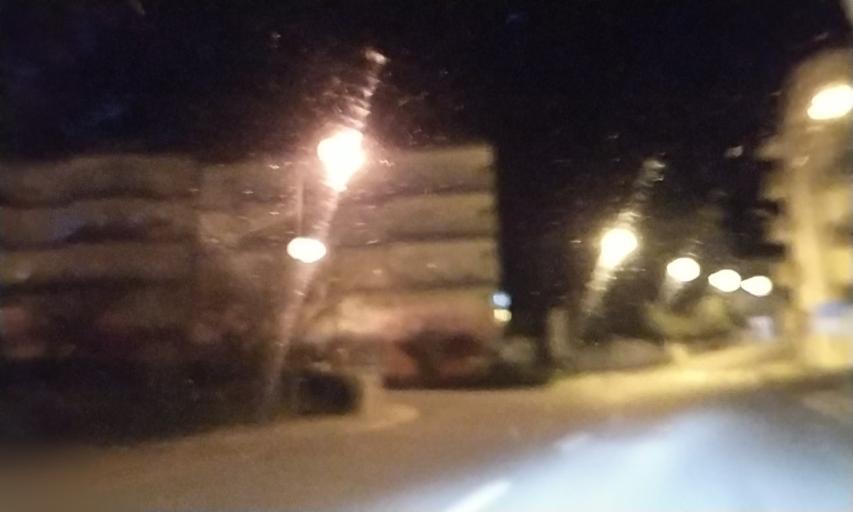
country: PT
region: Castelo Branco
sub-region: Concelho do Fundao
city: Fundao
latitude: 40.1369
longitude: -7.5051
